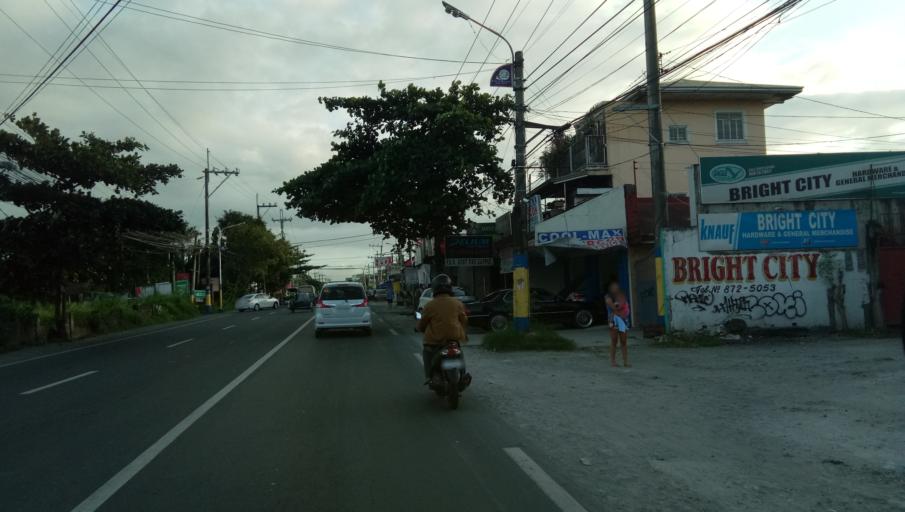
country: PH
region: Calabarzon
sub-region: Province of Cavite
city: Imus
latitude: 14.3811
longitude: 120.9787
